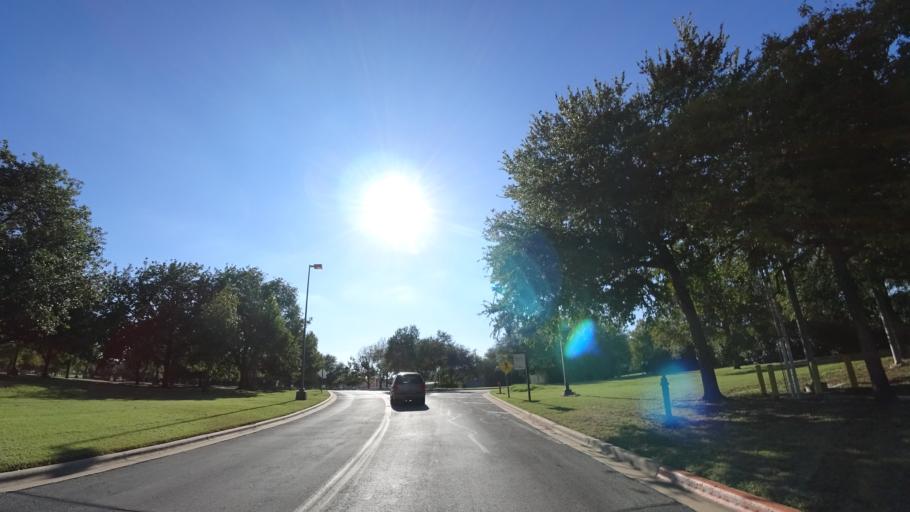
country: US
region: Texas
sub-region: Travis County
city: Austin
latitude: 30.2167
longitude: -97.7239
